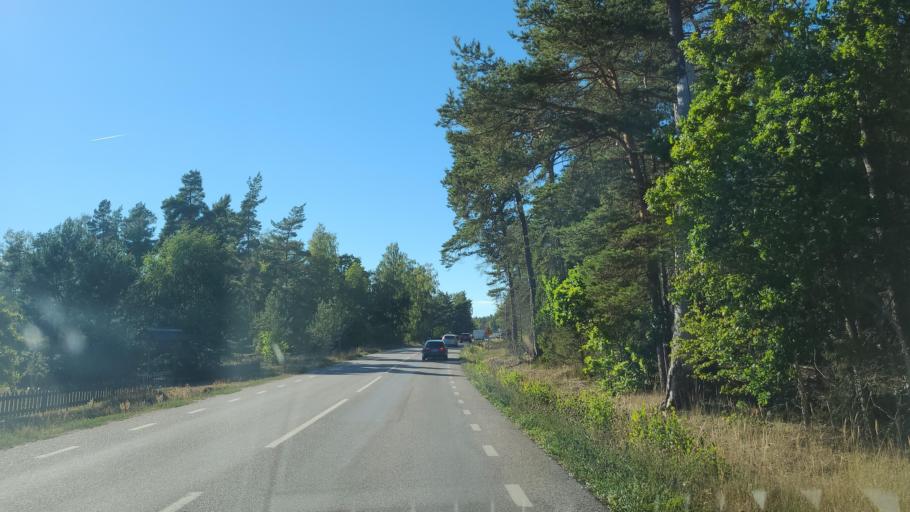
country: SE
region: Kalmar
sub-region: Borgholms Kommun
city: Borgholm
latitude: 57.2598
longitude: 17.0372
